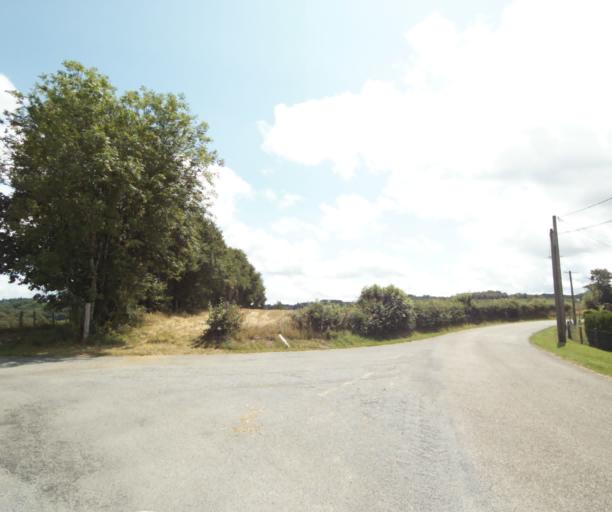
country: FR
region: Limousin
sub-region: Departement de la Correze
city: Sainte-Fortunade
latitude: 45.2103
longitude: 1.8100
